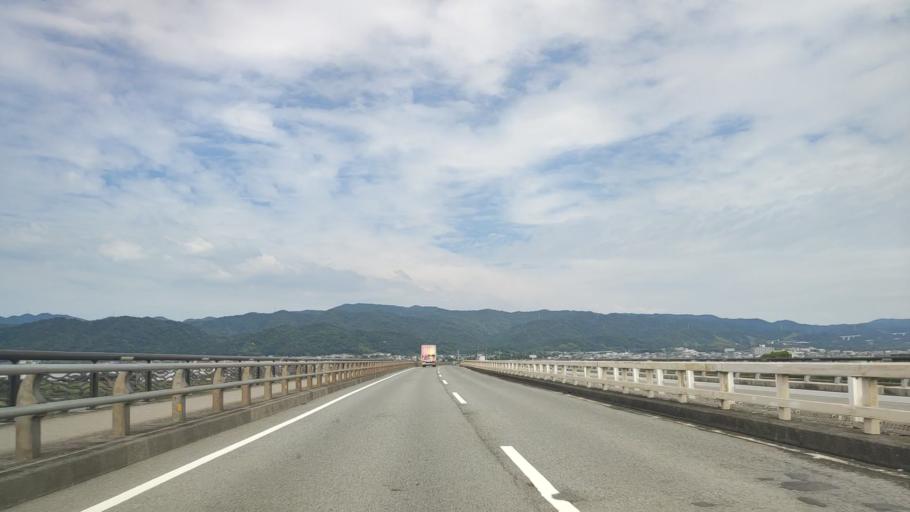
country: JP
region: Wakayama
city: Wakayama-shi
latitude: 34.2513
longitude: 135.2193
